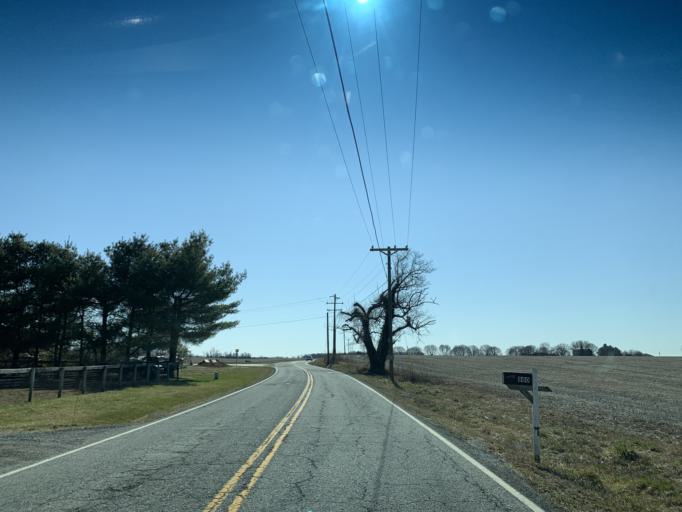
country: US
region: Maryland
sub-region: Cecil County
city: Charlestown
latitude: 39.4493
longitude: -75.9007
